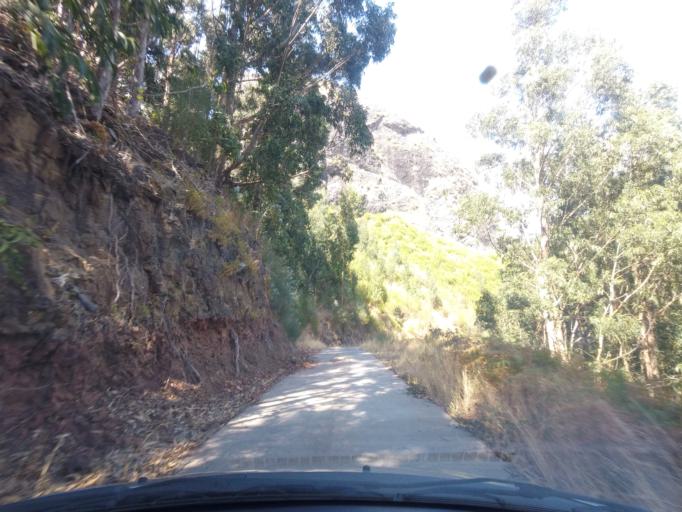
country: PT
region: Madeira
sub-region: Sao Vicente
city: Sao Vicente
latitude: 32.7409
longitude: -17.0273
